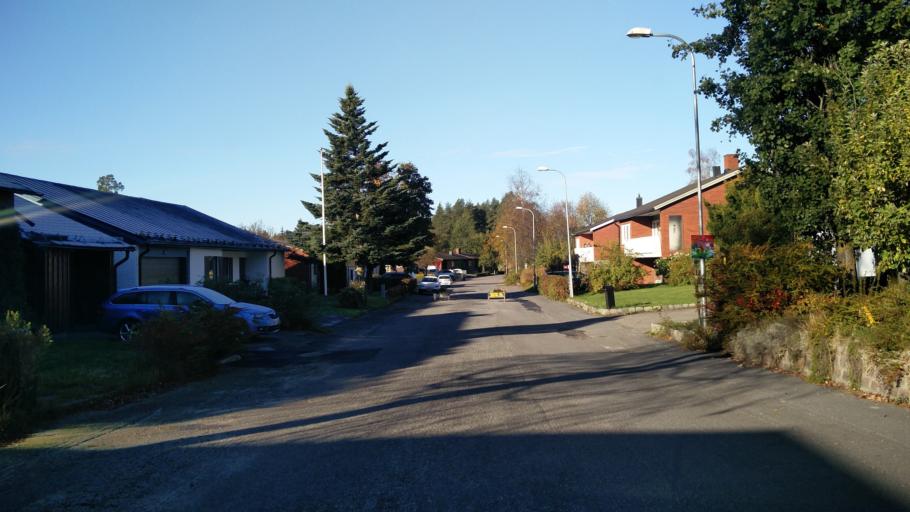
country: SE
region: Vaesternorrland
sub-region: Sundsvalls Kommun
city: Sundsvall
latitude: 62.4078
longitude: 17.2573
